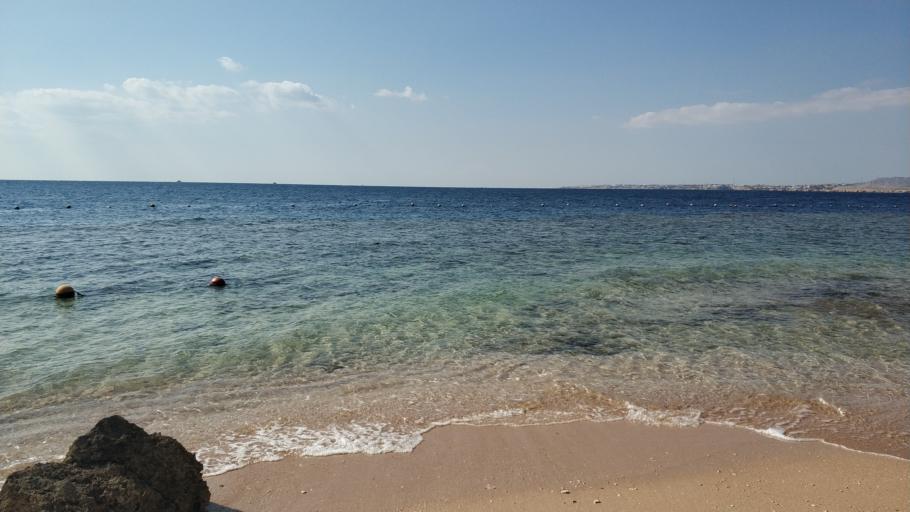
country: EG
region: South Sinai
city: Sharm el-Sheikh
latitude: 27.9148
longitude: 34.3636
